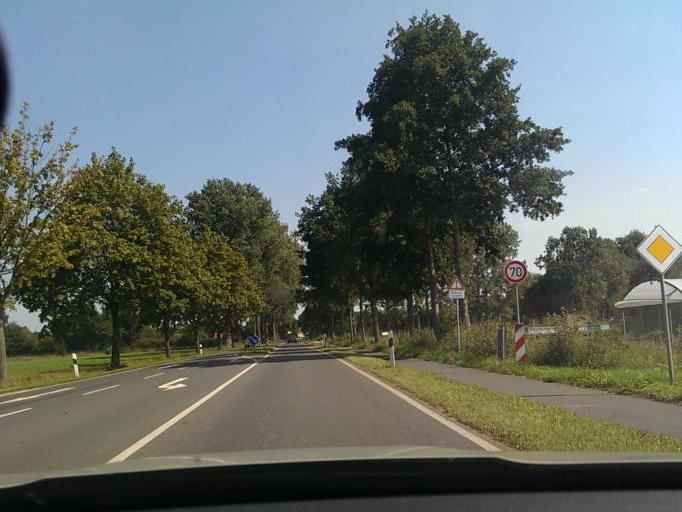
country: DE
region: Lower Saxony
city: Langenhagen
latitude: 52.4545
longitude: 9.7815
